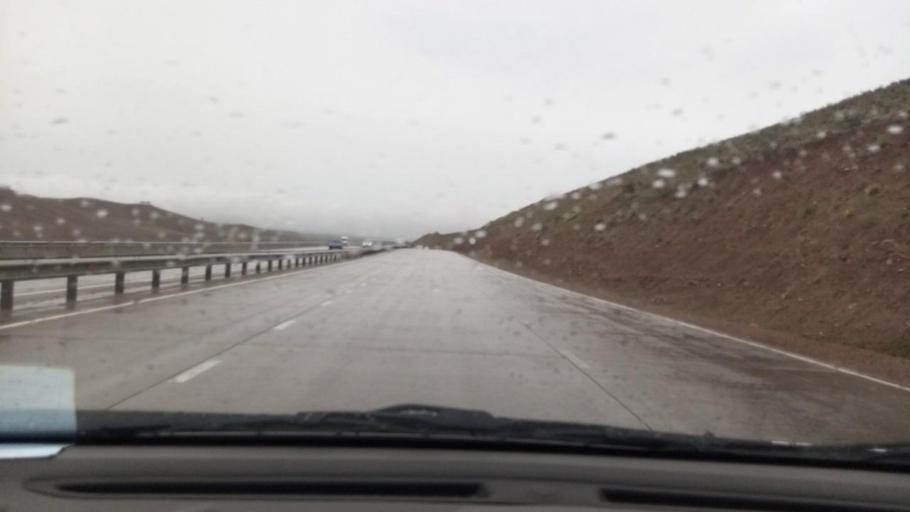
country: UZ
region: Namangan
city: Pop Shahri
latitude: 40.9307
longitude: 70.7046
